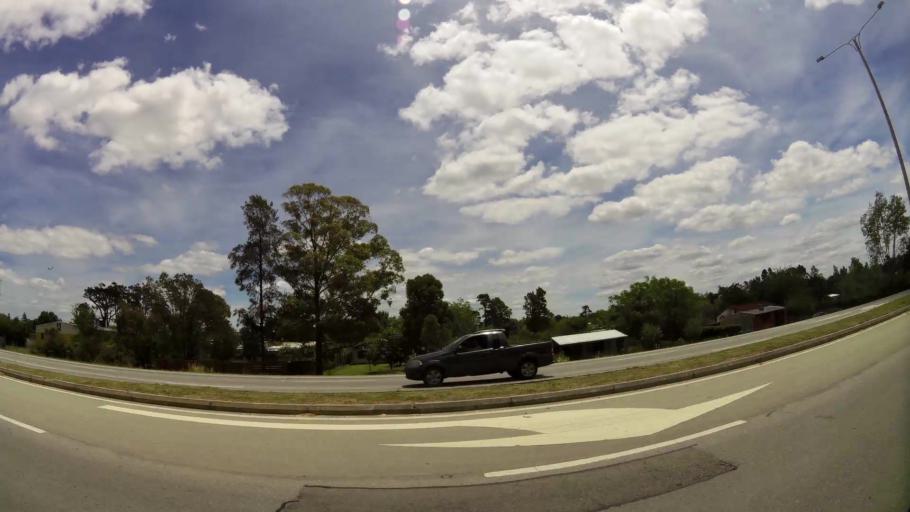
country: UY
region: Canelones
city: Colonia Nicolich
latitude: -34.8052
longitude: -55.9570
